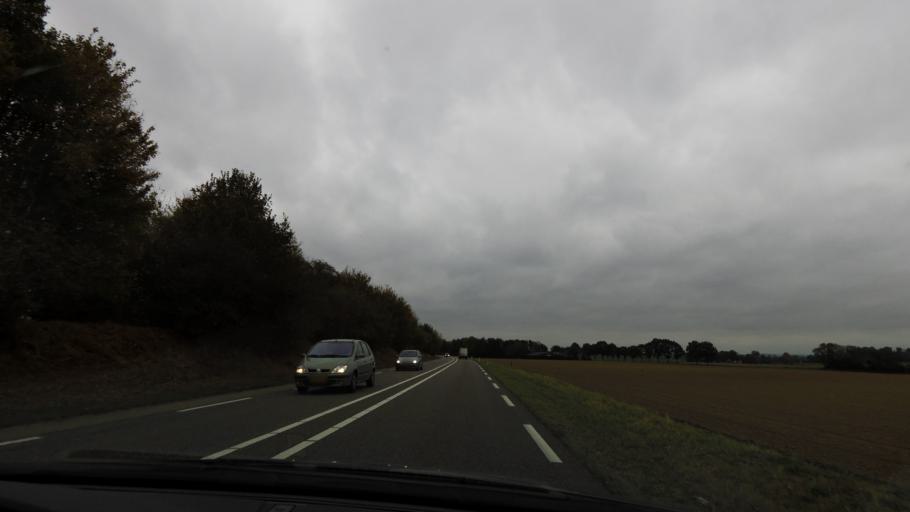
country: NL
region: Limburg
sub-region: Gemeente Schinnen
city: Amstenrade
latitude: 50.9539
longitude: 5.9247
